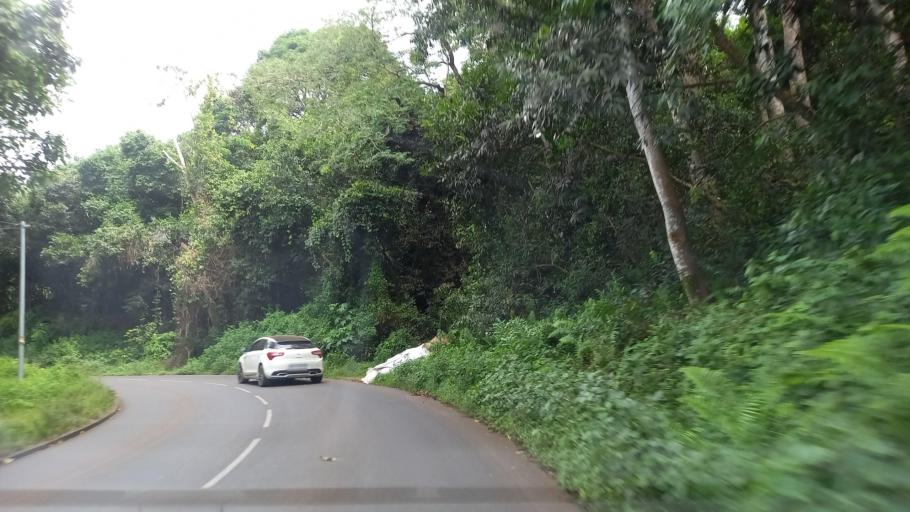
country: YT
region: Dembeni
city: Dembeni
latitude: -12.7867
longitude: 45.1656
